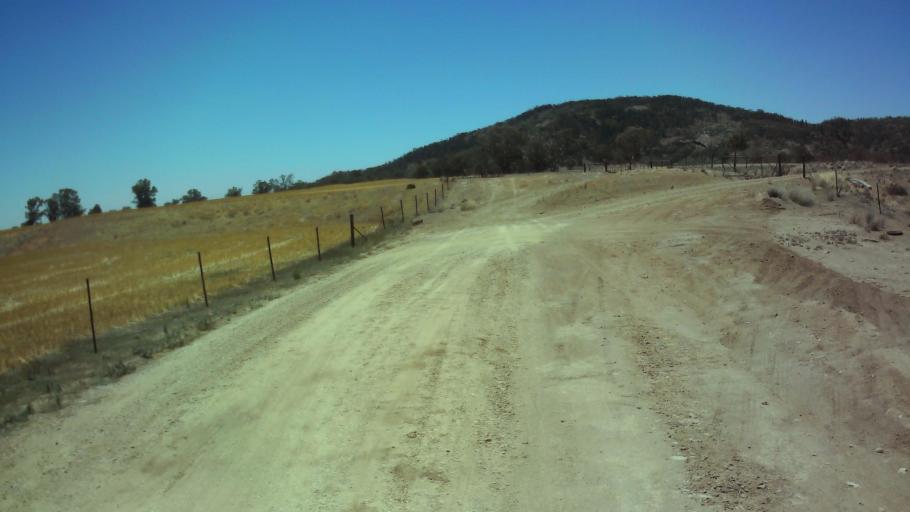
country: AU
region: New South Wales
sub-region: Weddin
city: Grenfell
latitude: -33.8536
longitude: 148.1081
